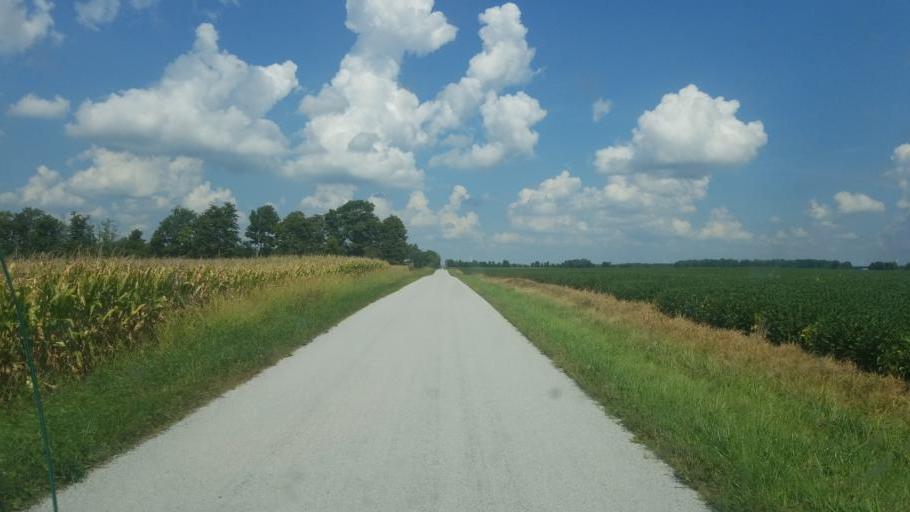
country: US
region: Ohio
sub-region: Hardin County
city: Ada
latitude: 40.7347
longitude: -83.7098
